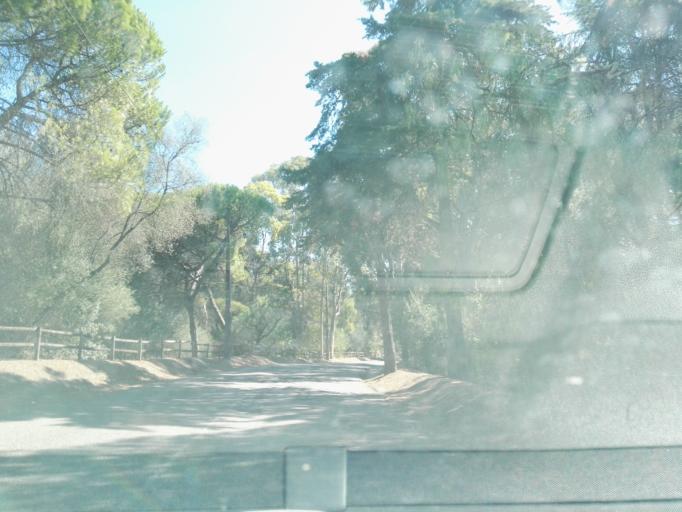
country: PT
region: Lisbon
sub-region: Oeiras
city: Alges
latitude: 38.7270
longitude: -9.2001
